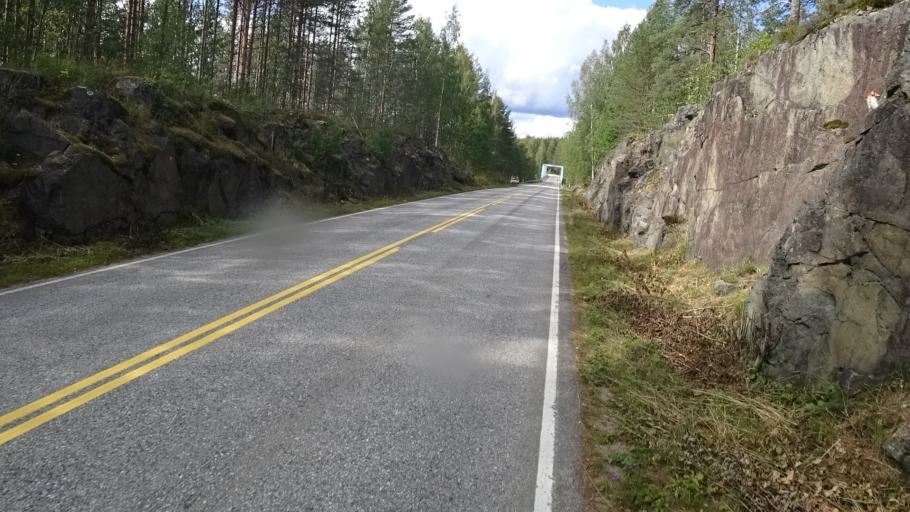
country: FI
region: North Karelia
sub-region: Joensuu
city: Ilomantsi
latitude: 62.6200
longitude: 31.2010
